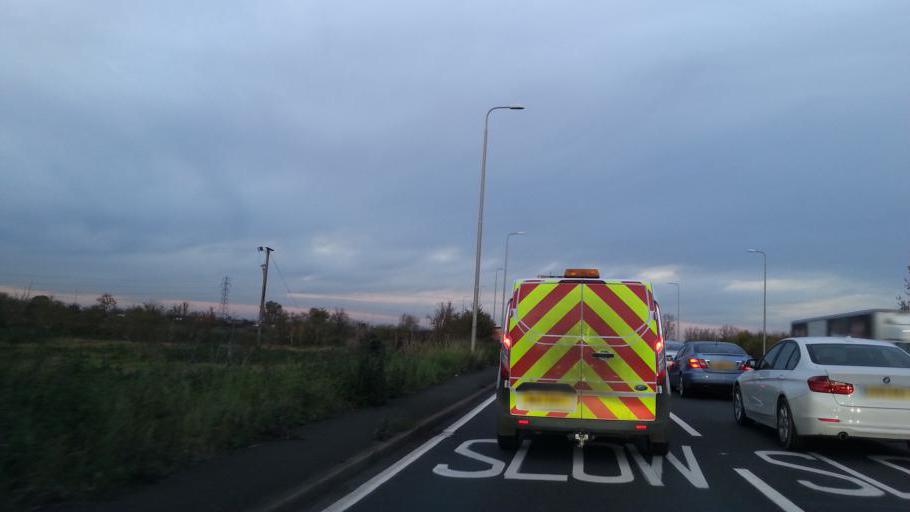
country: GB
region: England
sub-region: Central Bedfordshire
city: Tempsford
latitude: 52.1727
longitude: -0.3004
